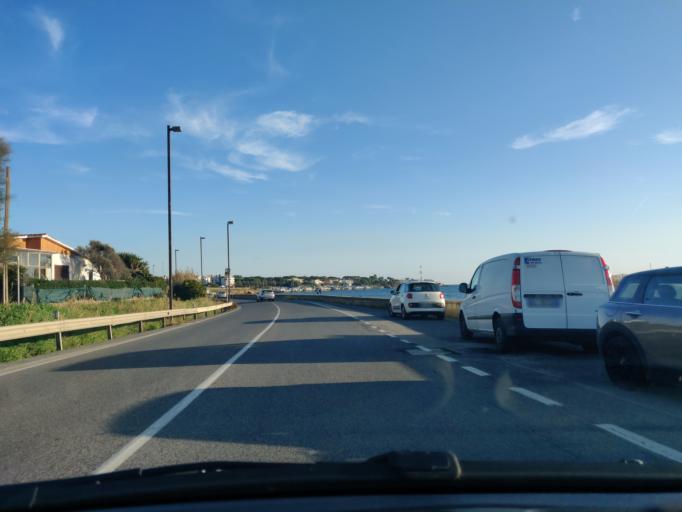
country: IT
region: Latium
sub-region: Citta metropolitana di Roma Capitale
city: Santa Marinella
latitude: 42.0404
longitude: 11.8290
